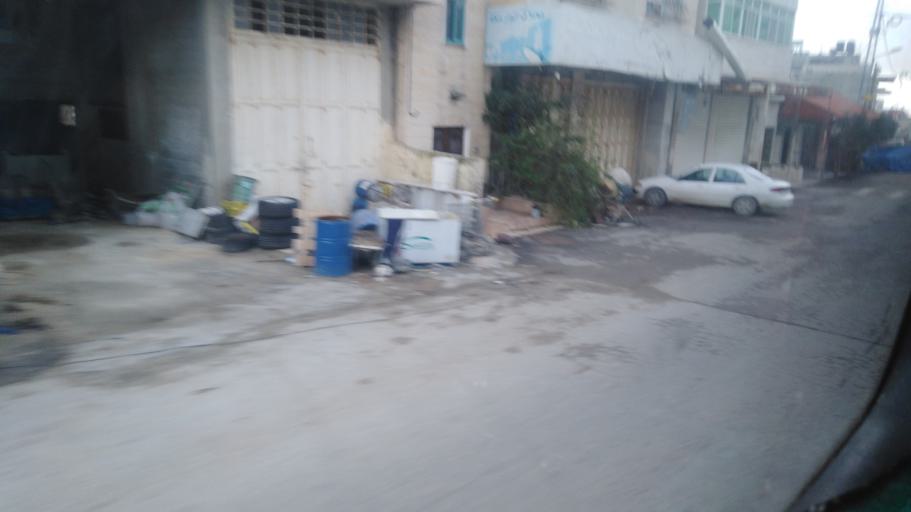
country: PS
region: West Bank
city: Hebron
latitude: 31.5270
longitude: 35.0775
